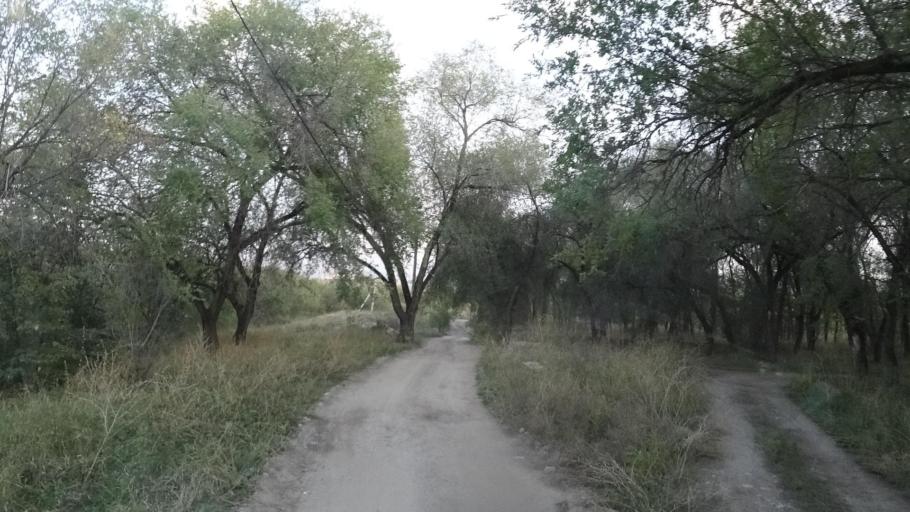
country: KZ
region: Almaty Oblysy
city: Pervomayskiy
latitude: 43.3364
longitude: 76.9983
